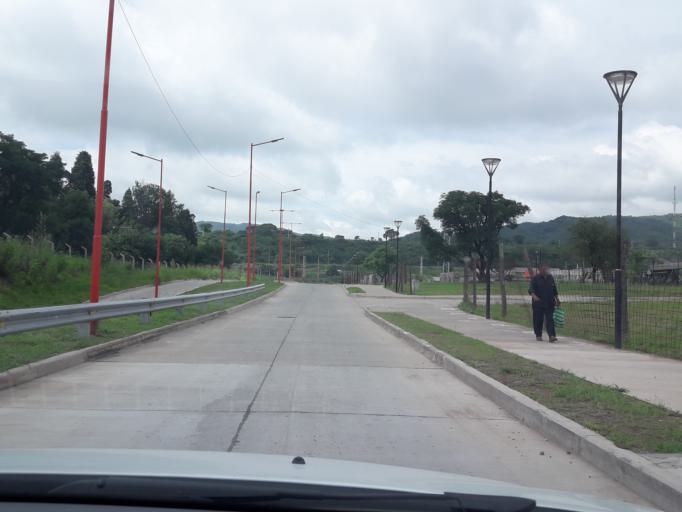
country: AR
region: Jujuy
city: San Salvador de Jujuy
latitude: -24.1810
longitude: -65.3275
